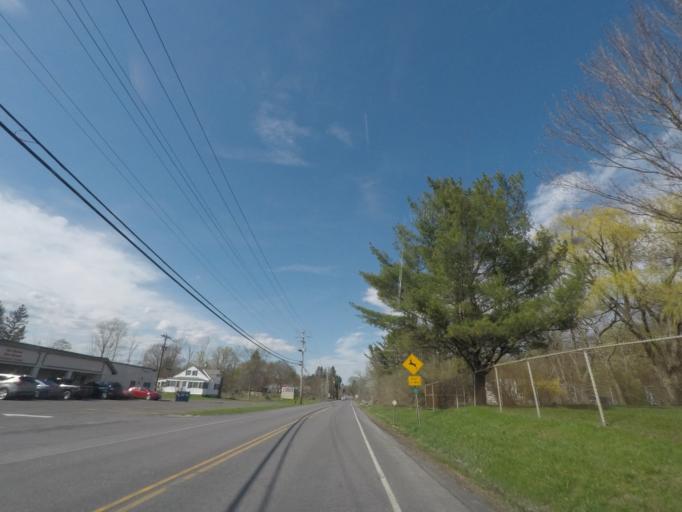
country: US
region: New York
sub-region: Greene County
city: Cairo
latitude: 42.4288
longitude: -74.0171
